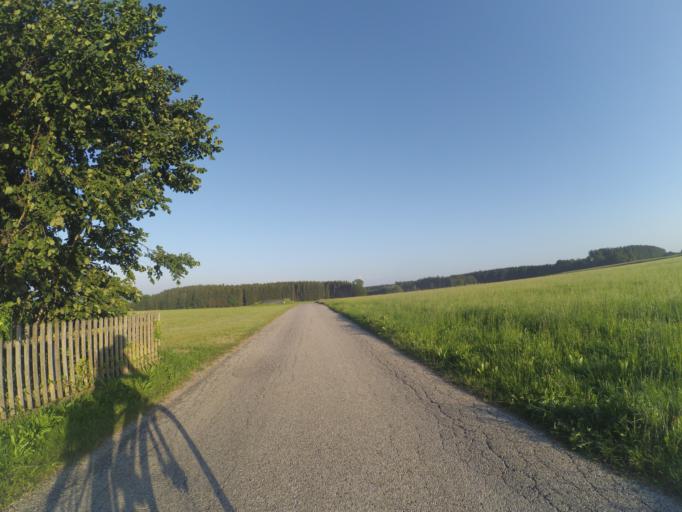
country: DE
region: Bavaria
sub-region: Swabia
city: Bad Worishofen
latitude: 48.0188
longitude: 10.5667
